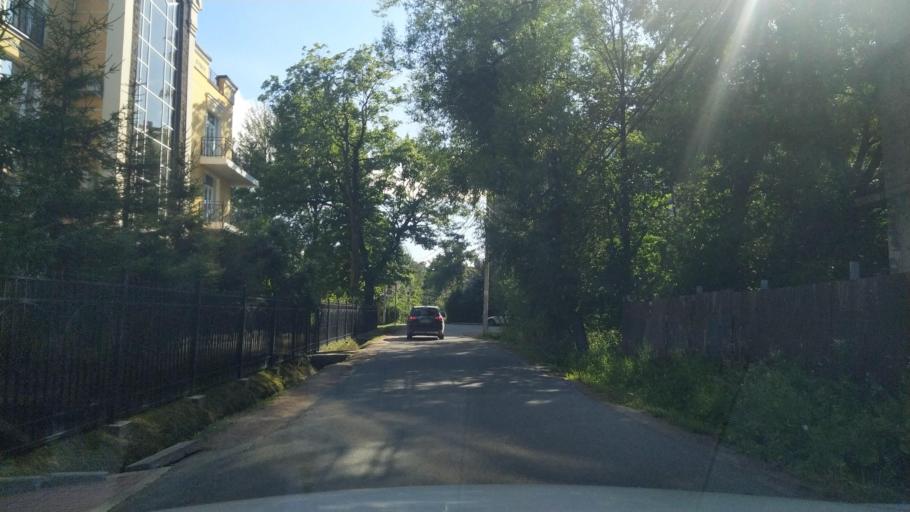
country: RU
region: St.-Petersburg
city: Kolomyagi
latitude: 60.0221
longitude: 30.2993
